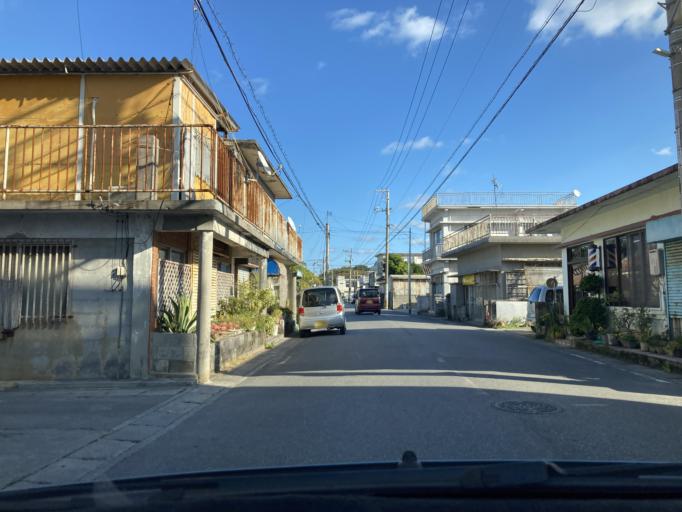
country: JP
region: Okinawa
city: Katsuren-haebaru
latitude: 26.3226
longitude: 127.9094
